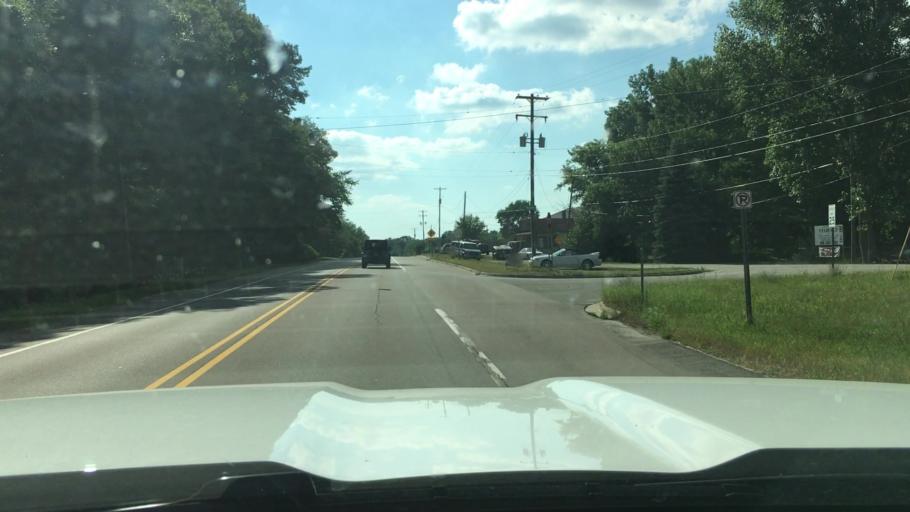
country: US
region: Michigan
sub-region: Kent County
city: Rockford
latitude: 43.0846
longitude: -85.4604
